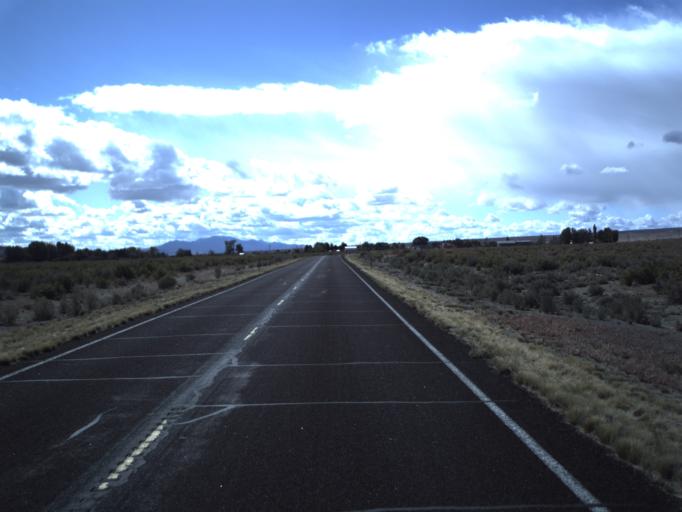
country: US
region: Nevada
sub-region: White Pine County
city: McGill
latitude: 38.9485
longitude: -114.0332
